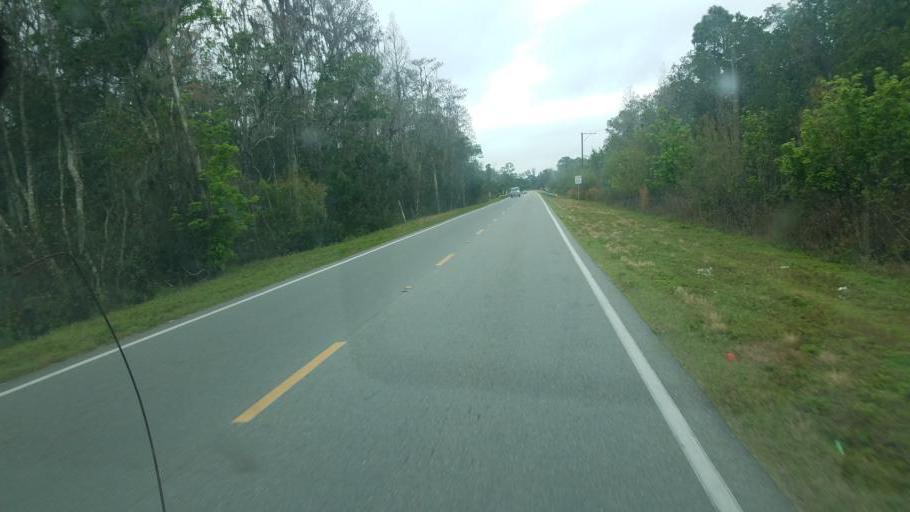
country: US
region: Florida
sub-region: Polk County
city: Polk City
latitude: 28.2586
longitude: -81.7968
